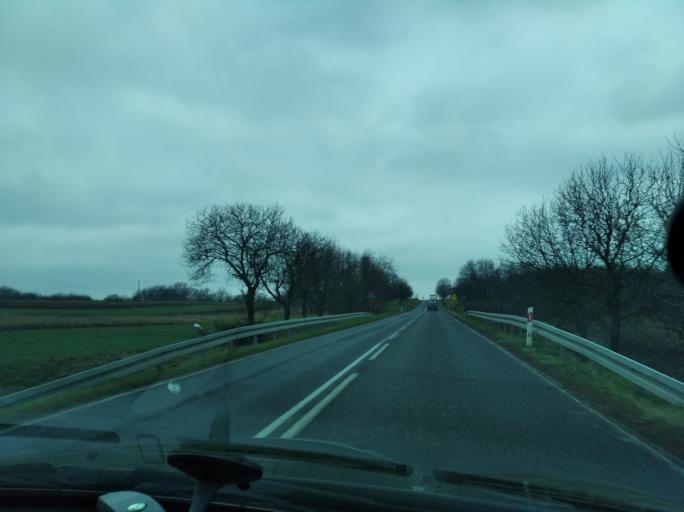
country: PL
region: Subcarpathian Voivodeship
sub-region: Powiat przeworski
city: Sietesz
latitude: 49.9976
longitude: 22.3653
